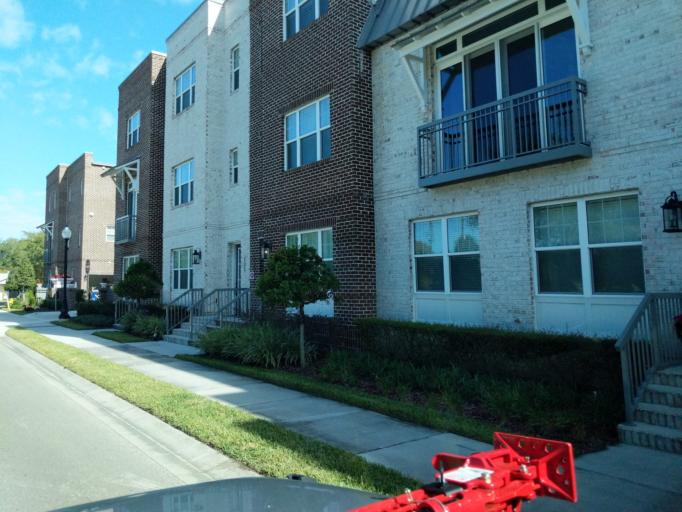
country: US
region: Florida
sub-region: Orange County
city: Winter Garden
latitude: 28.5636
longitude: -81.5919
